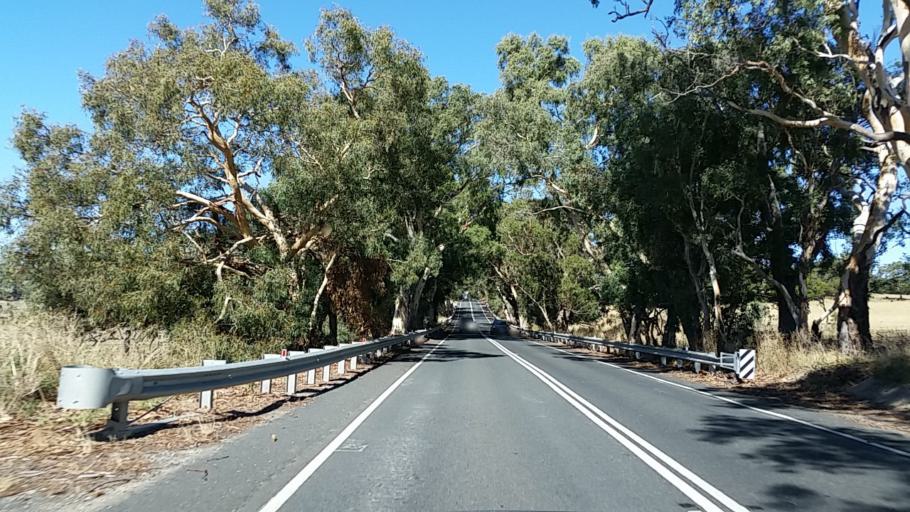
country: AU
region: South Australia
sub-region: Adelaide Hills
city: Birdwood
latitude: -34.7564
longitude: 139.0010
